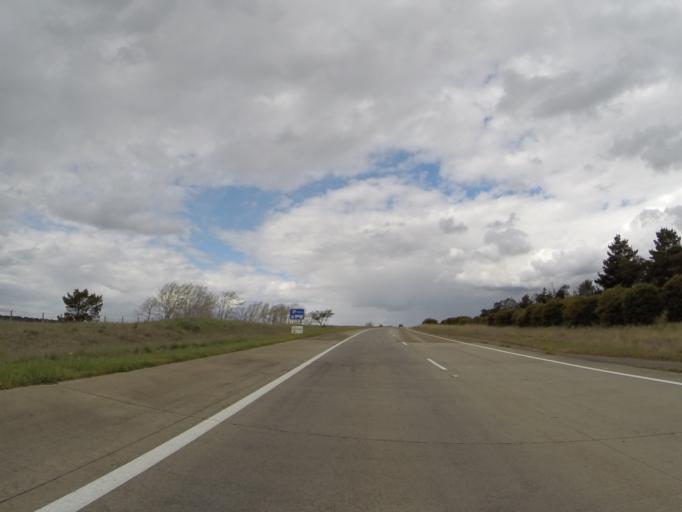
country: AU
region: New South Wales
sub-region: Goulburn Mulwaree
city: Goulburn
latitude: -34.8068
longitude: 149.5283
